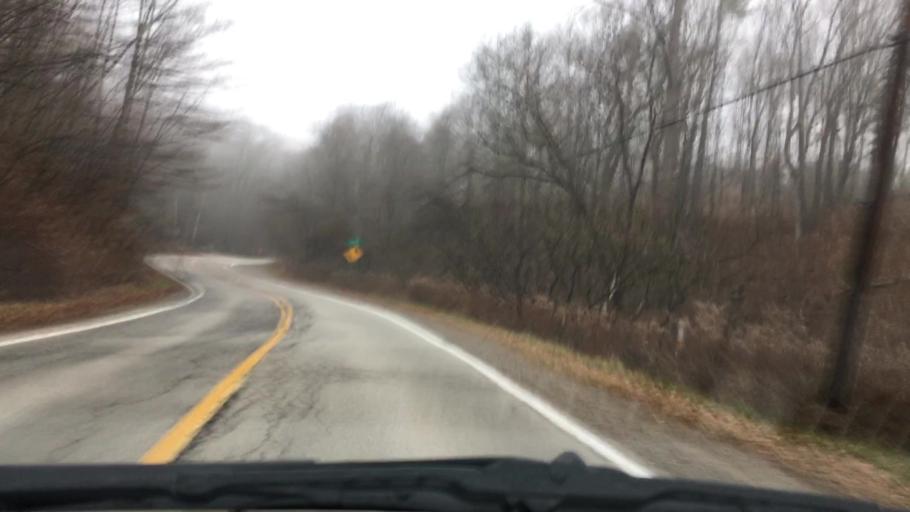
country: CA
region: Ontario
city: Hamilton
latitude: 43.3166
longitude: -79.8921
